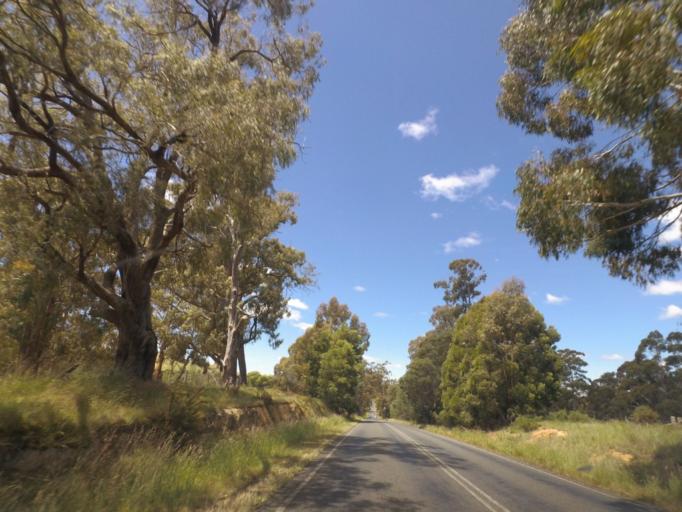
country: AU
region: Victoria
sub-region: Mount Alexander
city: Castlemaine
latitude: -37.3187
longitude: 144.2110
